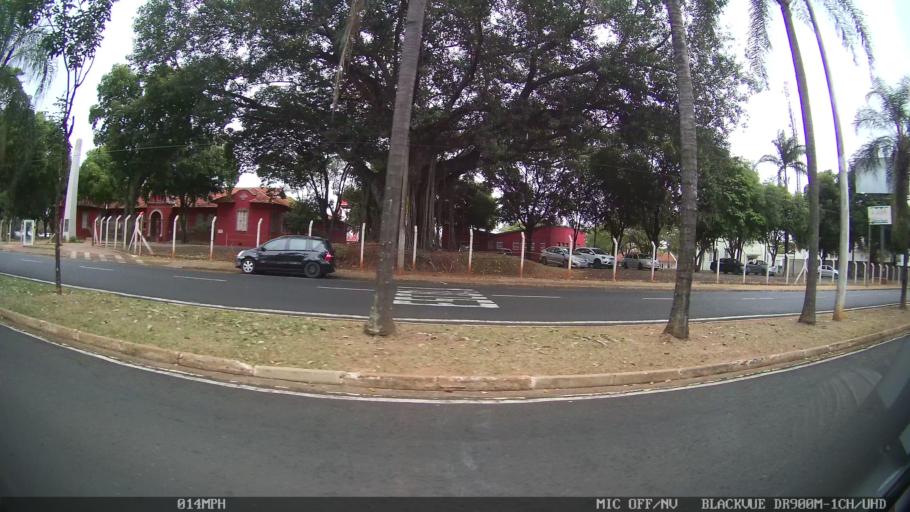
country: BR
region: Sao Paulo
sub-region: Sao Jose Do Rio Preto
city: Sao Jose do Rio Preto
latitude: -20.8371
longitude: -49.4008
